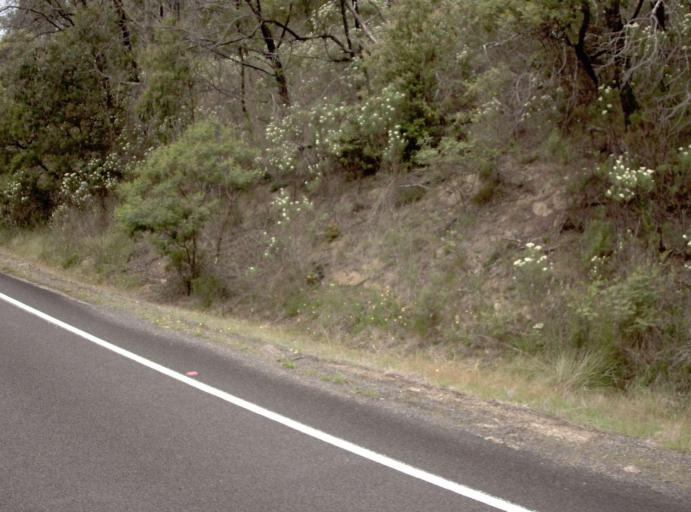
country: AU
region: New South Wales
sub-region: Bombala
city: Bombala
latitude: -37.2512
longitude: 149.2500
